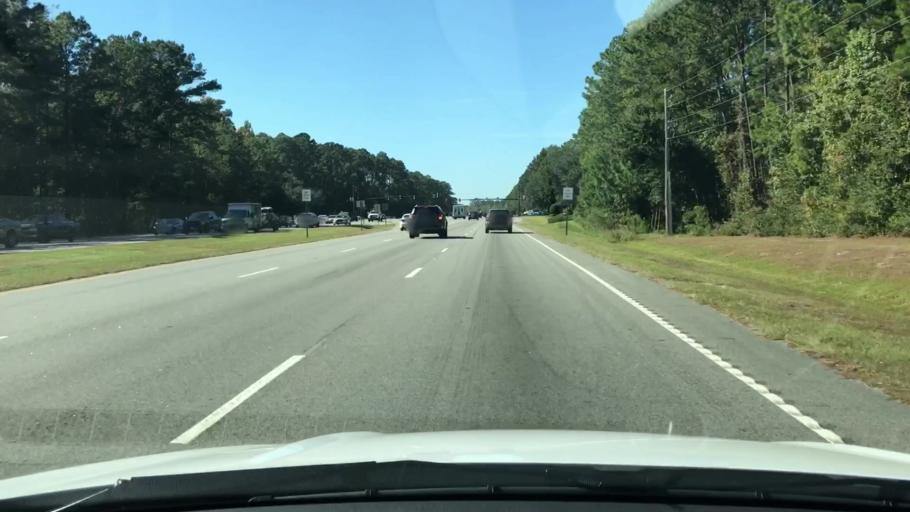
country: US
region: South Carolina
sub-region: Beaufort County
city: Bluffton
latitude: 32.2908
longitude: -80.9061
